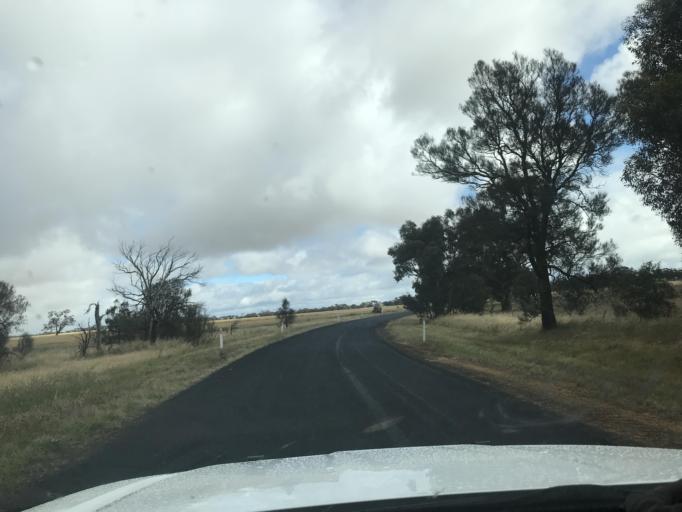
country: AU
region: South Australia
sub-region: Tatiara
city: Bordertown
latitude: -36.2029
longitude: 141.3100
